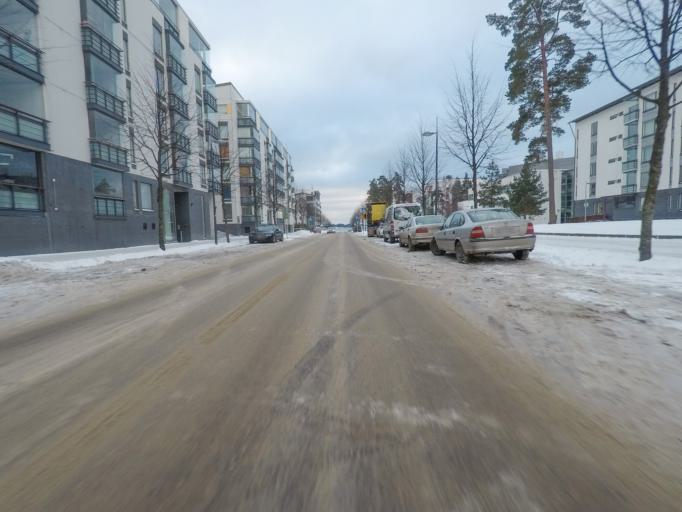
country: FI
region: Uusimaa
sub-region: Helsinki
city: Vantaa
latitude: 60.2038
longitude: 25.1483
